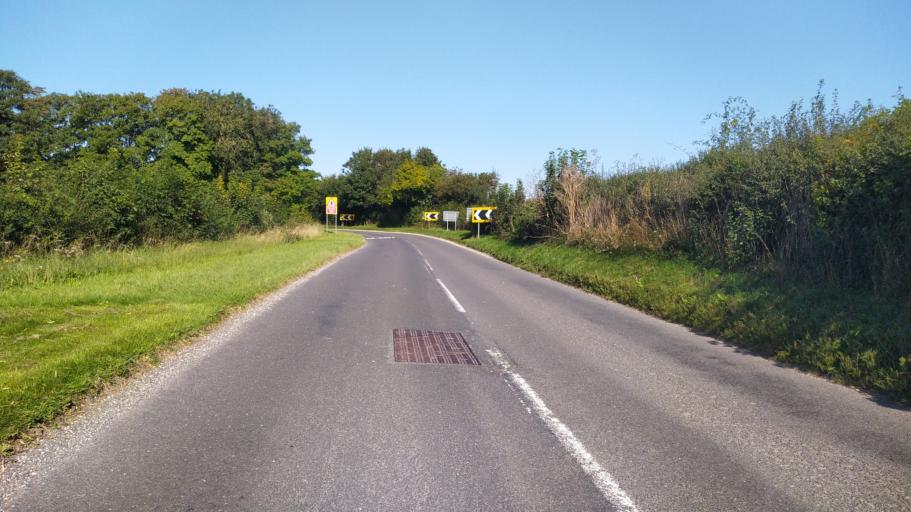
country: GB
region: England
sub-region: Hampshire
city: Abbotts Ann
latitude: 51.1654
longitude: -1.6005
